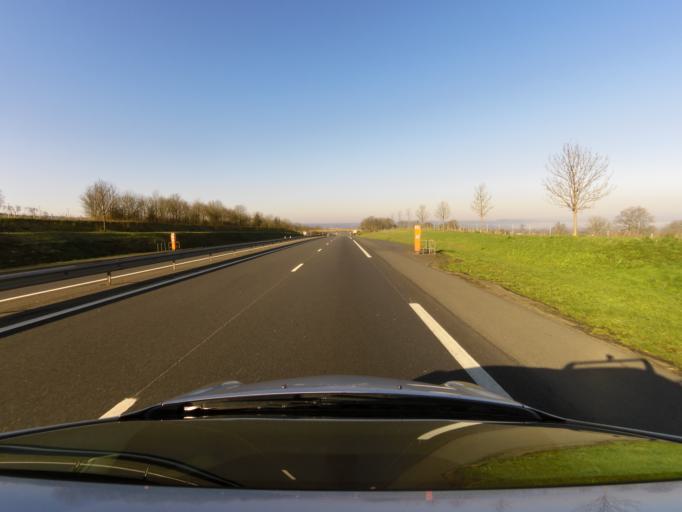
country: FR
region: Lower Normandy
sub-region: Departement du Calvados
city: Cahagnes
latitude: 49.0403
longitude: -0.8023
